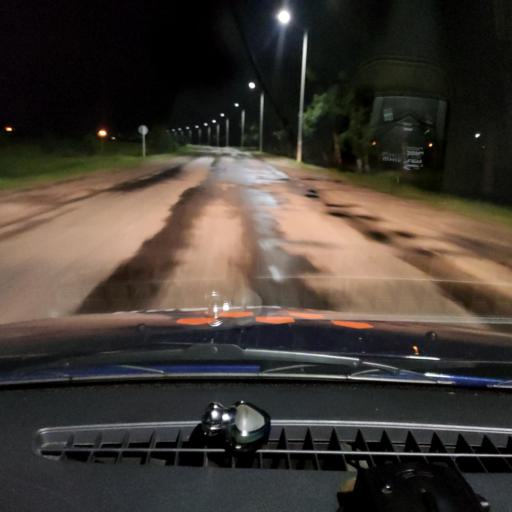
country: RU
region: Voronezj
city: Khrenovoye
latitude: 51.1174
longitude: 40.2633
